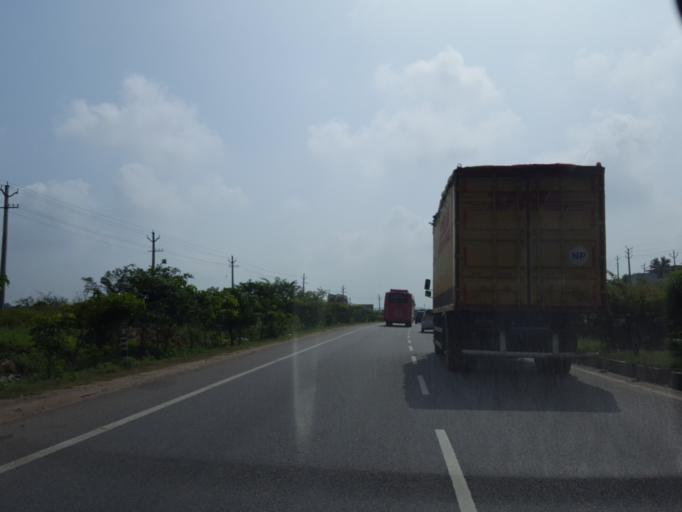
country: IN
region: Telangana
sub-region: Rangareddi
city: Ghatkesar
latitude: 17.2842
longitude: 78.7789
